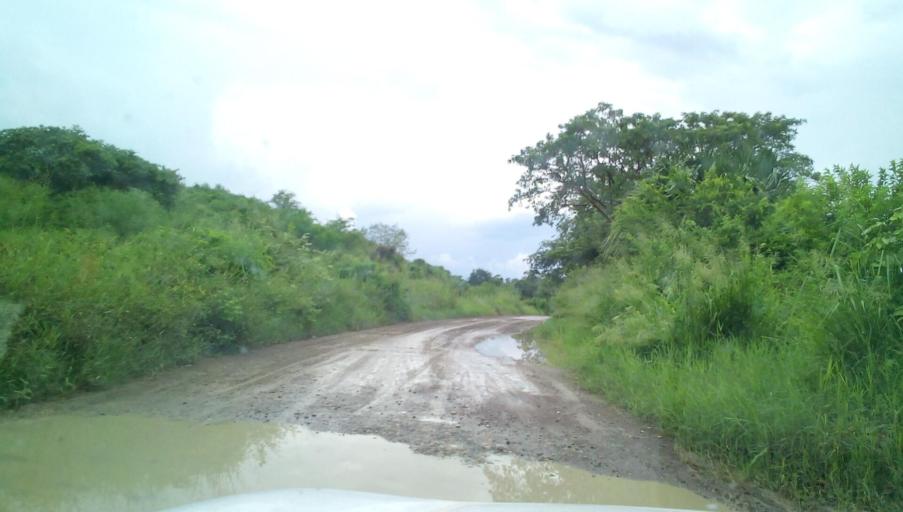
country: MX
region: Veracruz
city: Panuco
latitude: 21.8089
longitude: -98.1066
